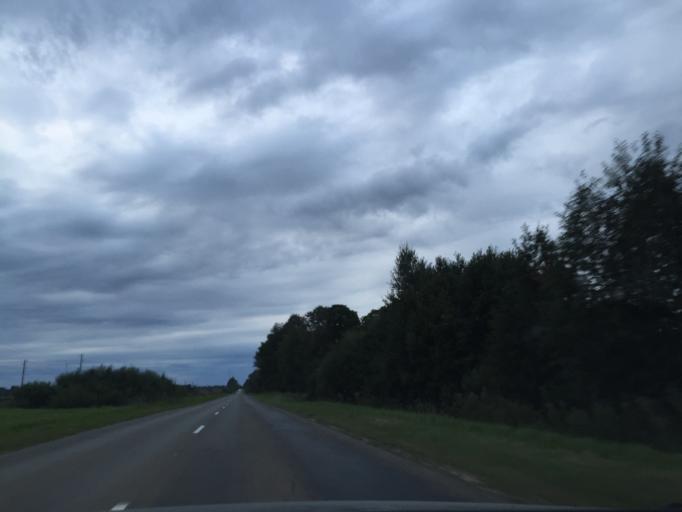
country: LV
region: Vecumnieki
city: Vecumnieki
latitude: 56.5229
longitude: 24.5560
